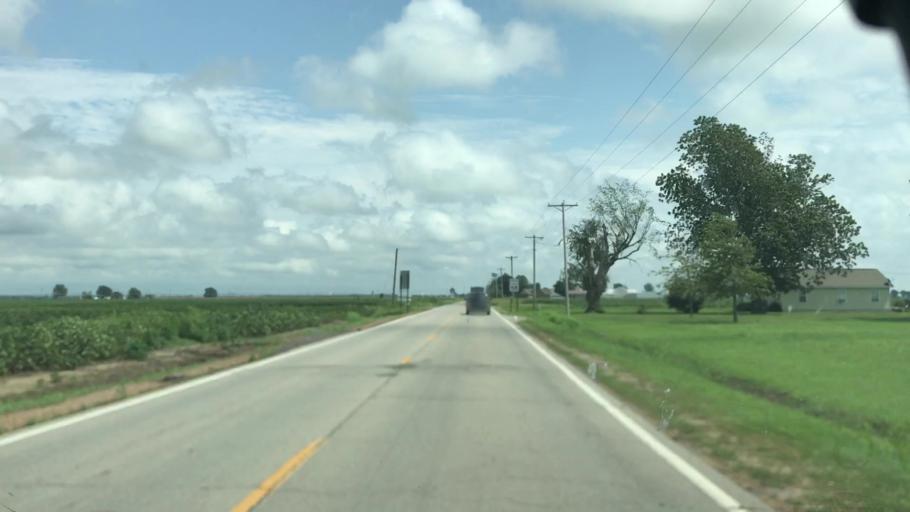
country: US
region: Missouri
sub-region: Pemiscot County
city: Hayti
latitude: 36.1759
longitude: -89.7325
